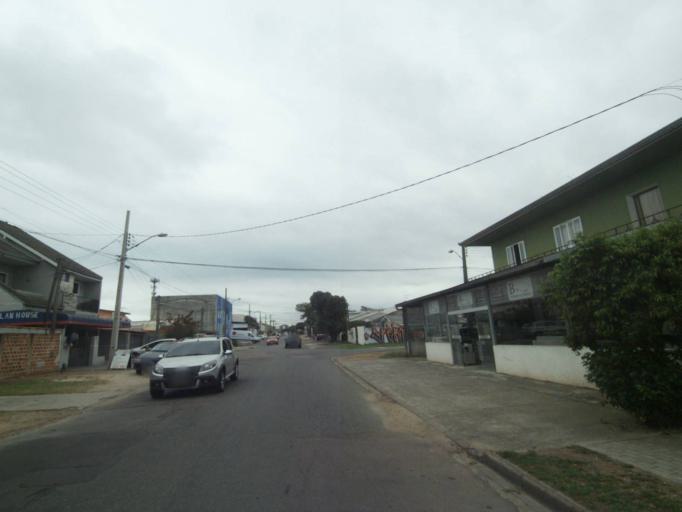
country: BR
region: Parana
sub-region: Sao Jose Dos Pinhais
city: Sao Jose dos Pinhais
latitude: -25.5428
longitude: -49.2528
